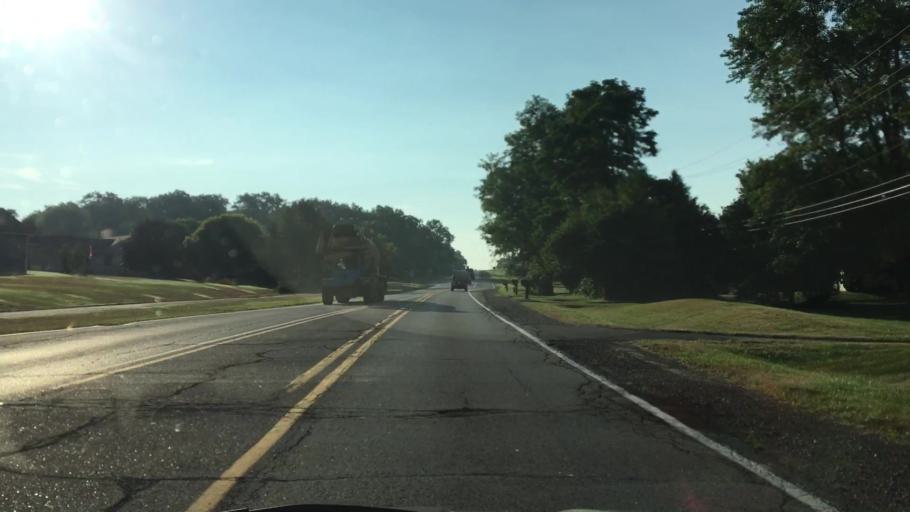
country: US
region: Michigan
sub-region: Oakland County
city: South Lyon
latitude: 42.5165
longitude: -83.6386
